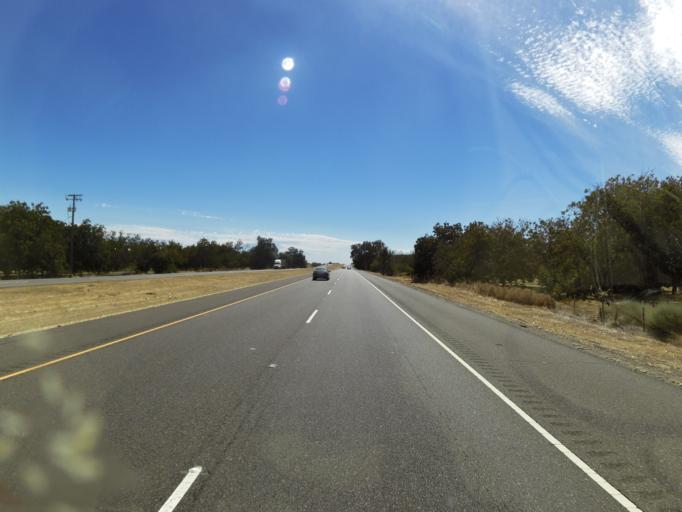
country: US
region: California
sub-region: Yolo County
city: Winters
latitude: 38.5039
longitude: -121.9517
